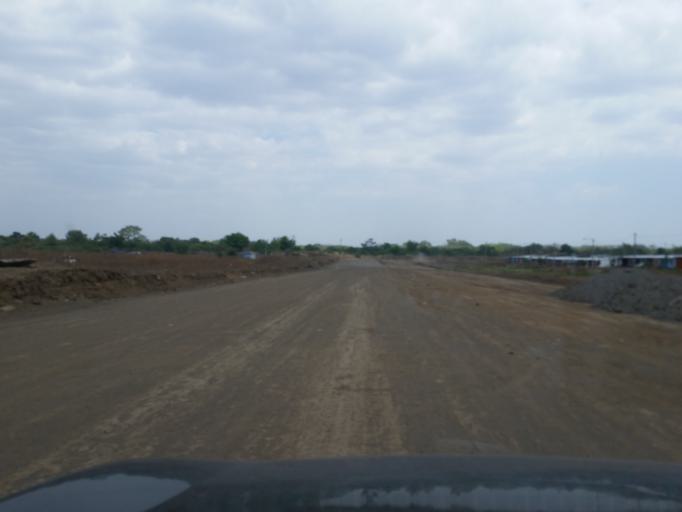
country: NI
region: Managua
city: Tipitapa
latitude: 12.1344
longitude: -86.1569
